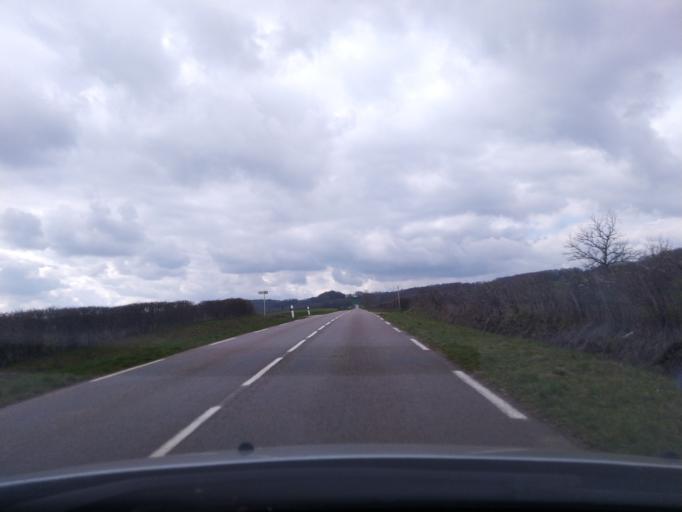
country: FR
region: Bourgogne
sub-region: Departement de l'Yonne
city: Avallon
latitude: 47.5350
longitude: 4.0152
